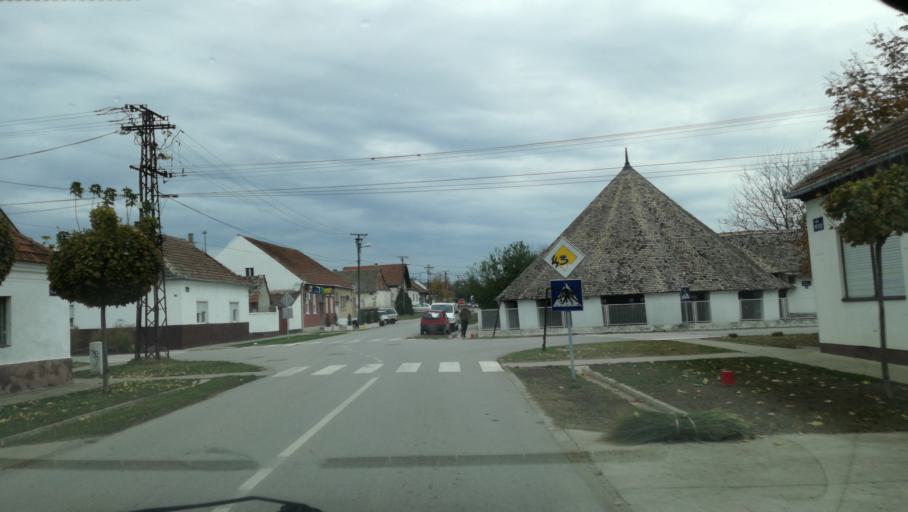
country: RS
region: Autonomna Pokrajina Vojvodina
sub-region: Severnobanatski Okrug
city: Kikinda
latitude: 45.8238
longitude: 20.4535
